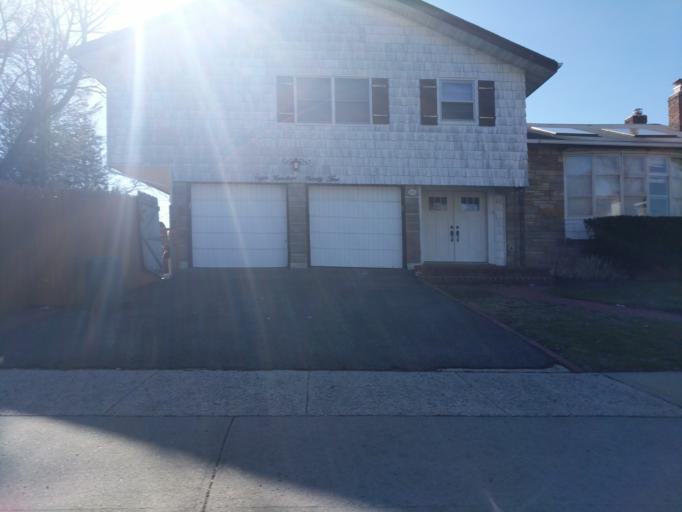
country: US
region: New York
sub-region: Nassau County
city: South Valley Stream
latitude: 40.6493
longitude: -73.7241
